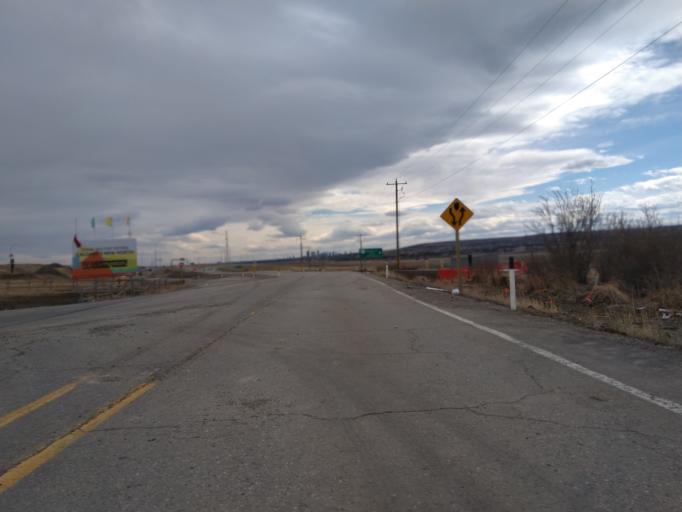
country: CA
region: Alberta
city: Airdrie
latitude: 51.1795
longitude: -114.0714
